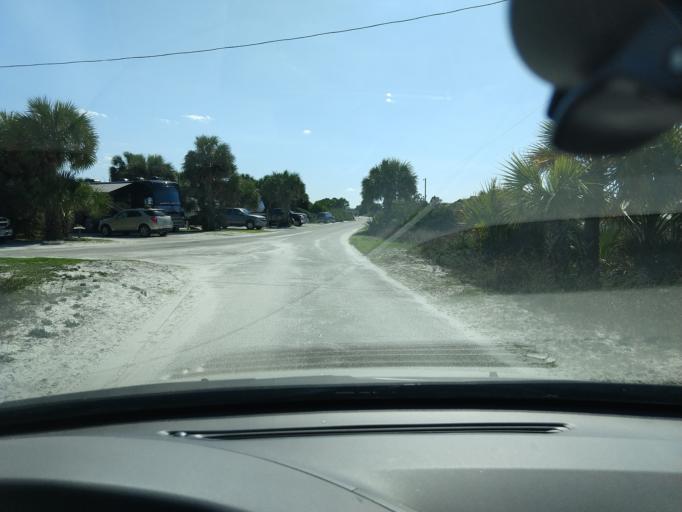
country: US
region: Florida
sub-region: Gulf County
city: Port Saint Joe
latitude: 29.7737
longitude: -85.4064
